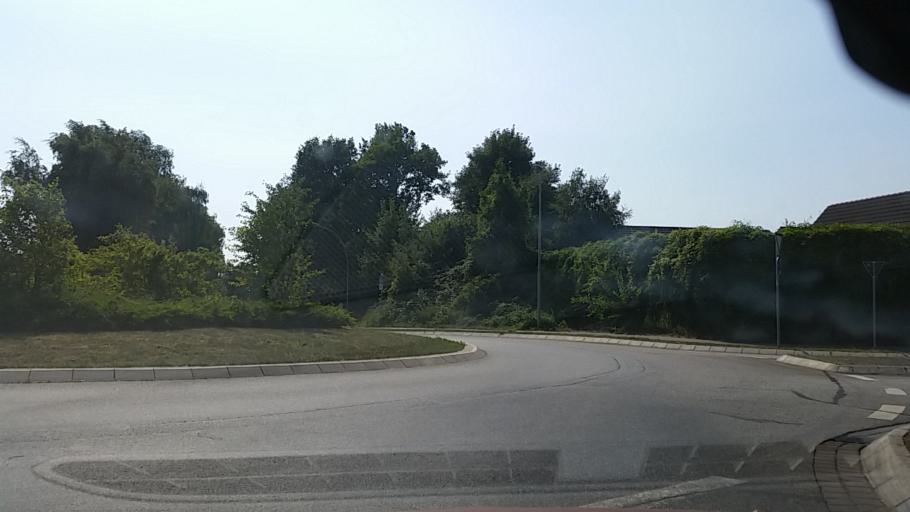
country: DE
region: Schleswig-Holstein
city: Glinde
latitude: 53.5454
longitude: 10.2268
